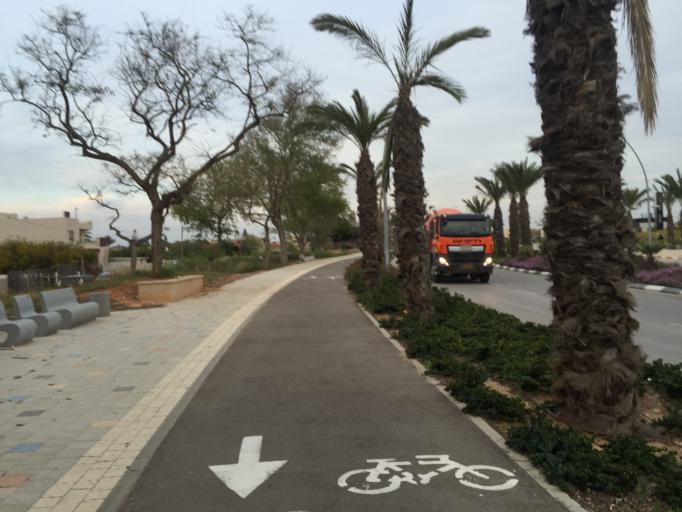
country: IL
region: Haifa
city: Qesarya
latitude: 32.5053
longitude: 34.9162
